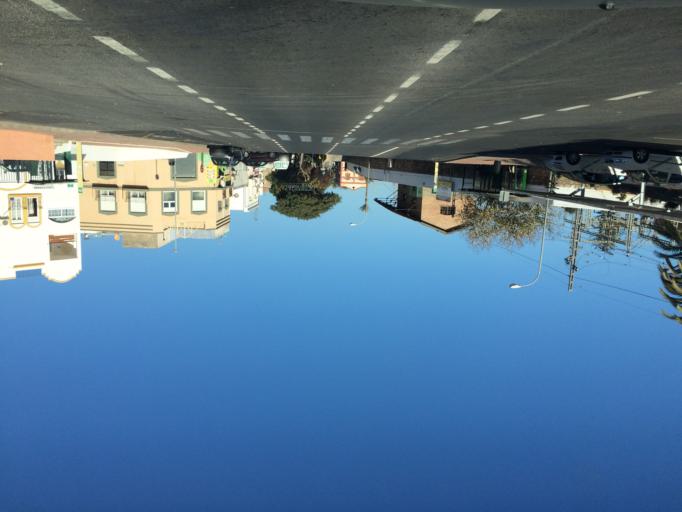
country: ES
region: Andalusia
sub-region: Provincia de Almeria
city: Huercal de Almeria
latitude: 36.8817
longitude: -2.4355
